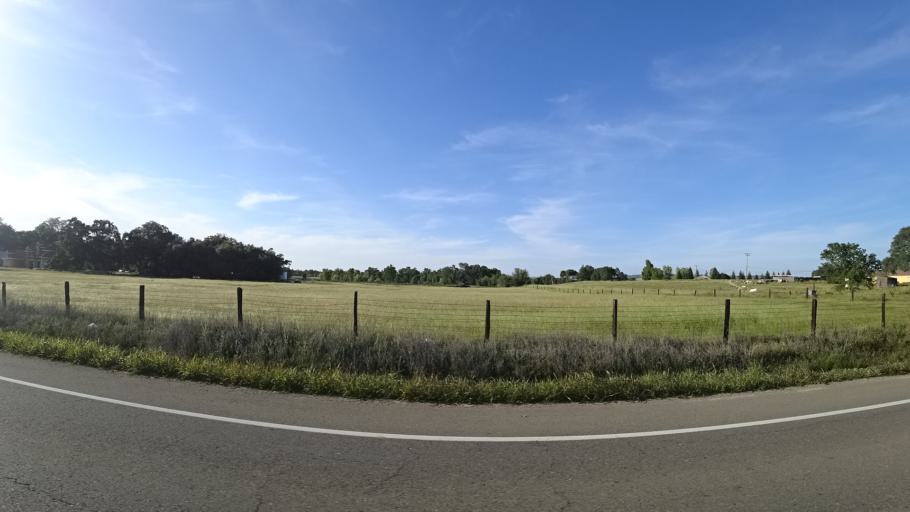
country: US
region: California
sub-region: Placer County
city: Lincoln
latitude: 38.9265
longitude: -121.2700
